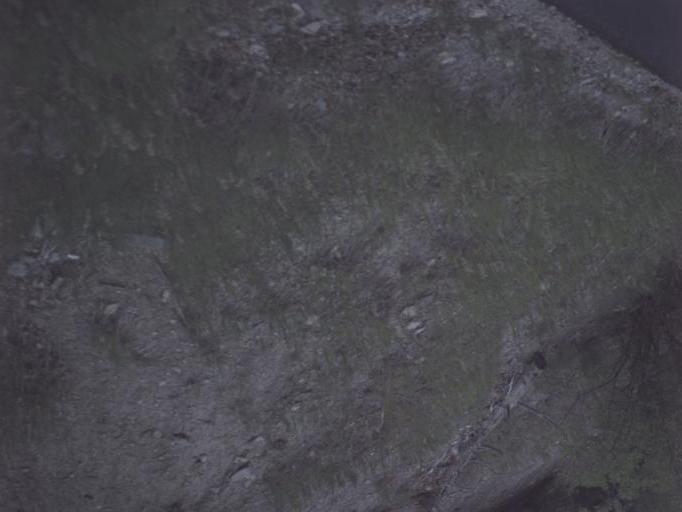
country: US
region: Utah
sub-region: Utah County
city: Cedar Hills
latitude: 40.4489
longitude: -111.6457
